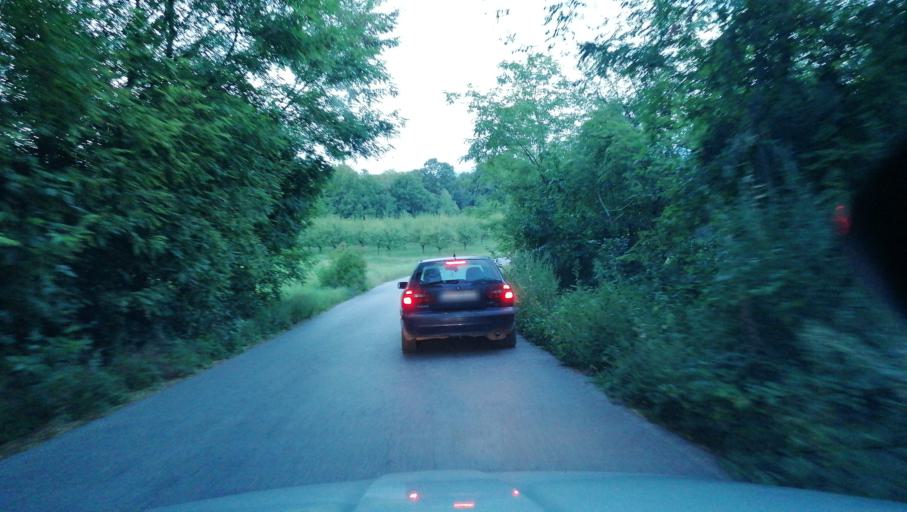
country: RS
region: Central Serbia
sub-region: Kolubarski Okrug
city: Valjevo
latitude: 44.2469
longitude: 19.8703
